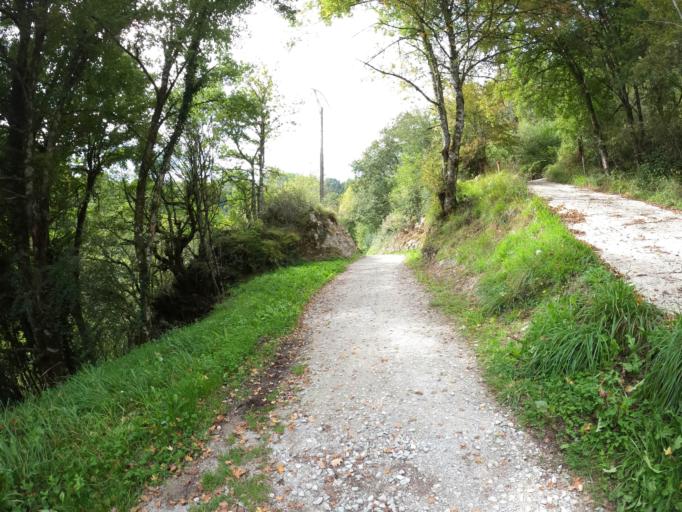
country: ES
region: Navarre
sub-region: Provincia de Navarra
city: Lekunberri
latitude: 42.9873
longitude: -1.8800
